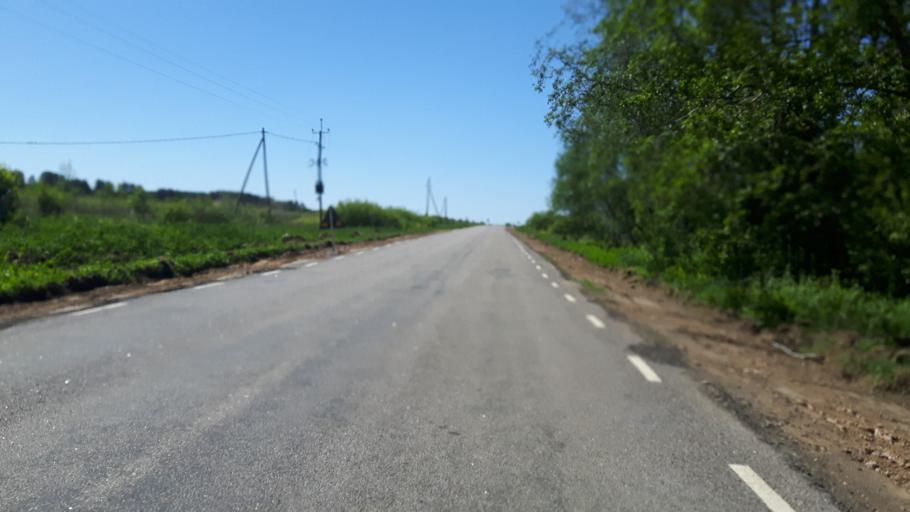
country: EE
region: Ida-Virumaa
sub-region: Narva-Joesuu linn
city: Narva-Joesuu
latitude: 59.4040
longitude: 27.9387
